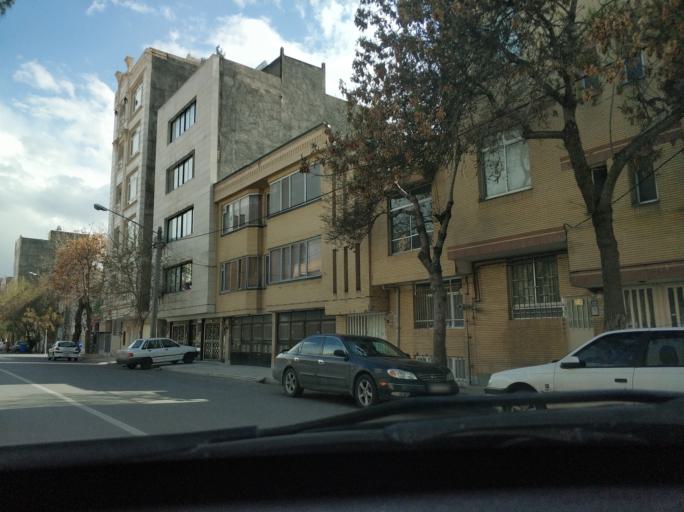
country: IR
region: Razavi Khorasan
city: Mashhad
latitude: 36.2719
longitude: 59.5908
